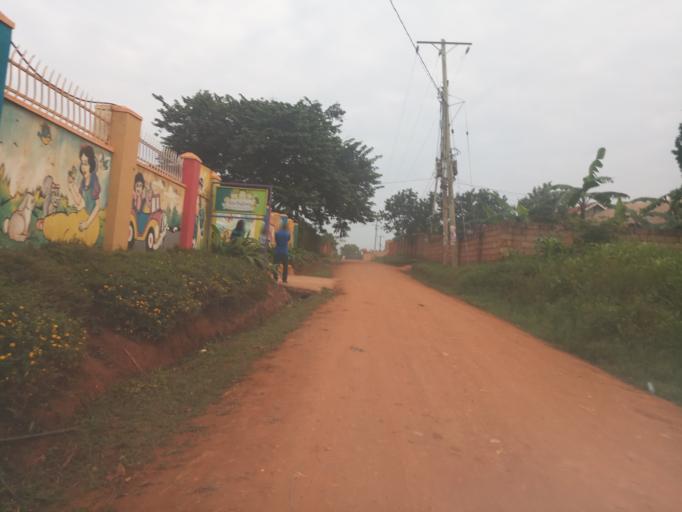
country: UG
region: Central Region
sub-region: Wakiso District
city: Kireka
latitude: 0.3915
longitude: 32.6358
